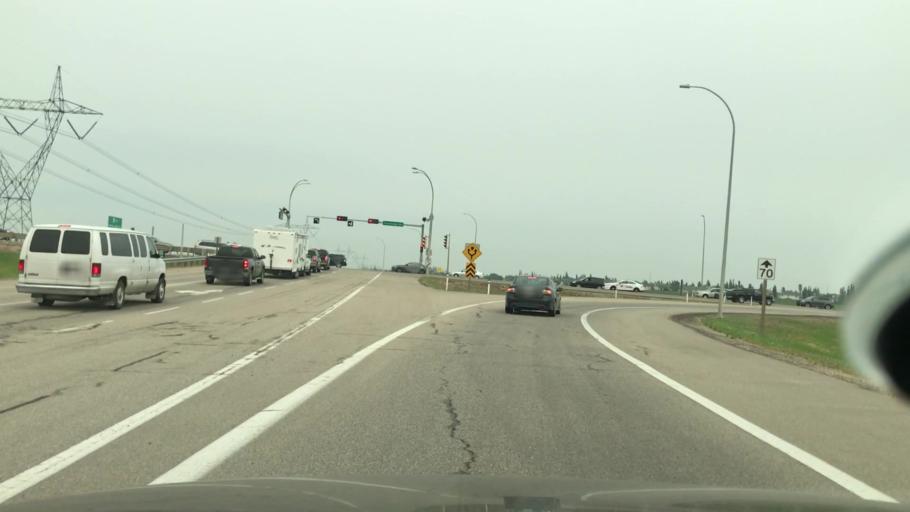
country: CA
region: Alberta
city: Devon
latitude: 53.4441
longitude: -113.5975
